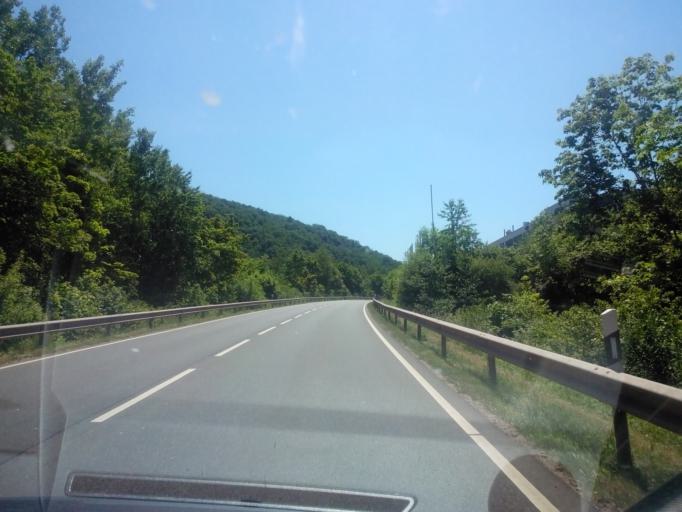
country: DE
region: Rheinland-Pfalz
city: Saarburg
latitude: 49.6004
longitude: 6.5396
